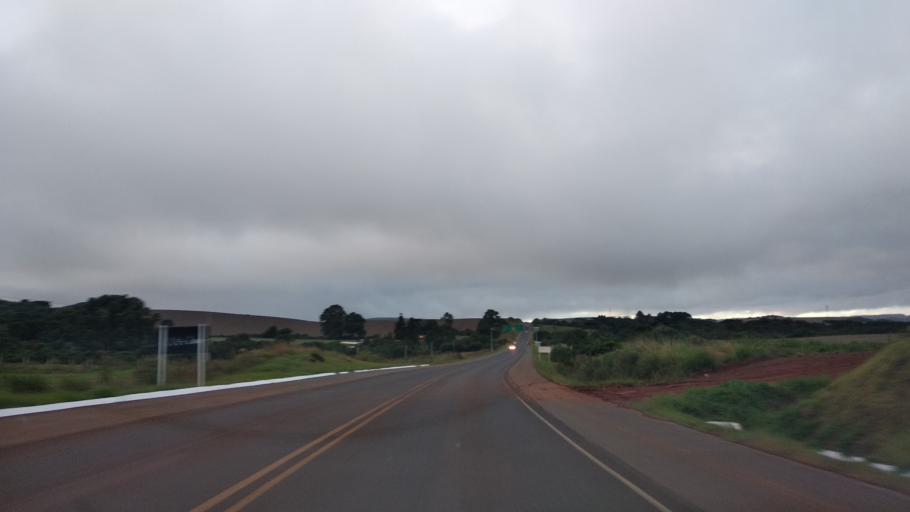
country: BR
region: Santa Catarina
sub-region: Campos Novos
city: Campos Novos
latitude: -27.3761
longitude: -51.0654
